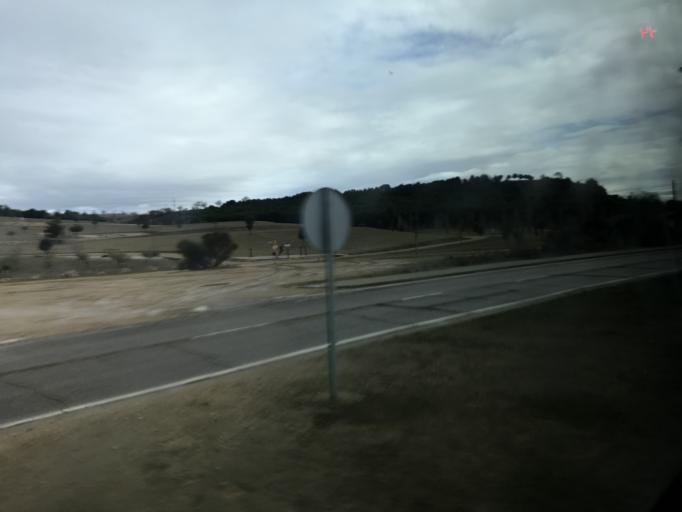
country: ES
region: Castille and Leon
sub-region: Provincia de Valladolid
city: Zaratan
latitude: 41.6511
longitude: -4.7613
